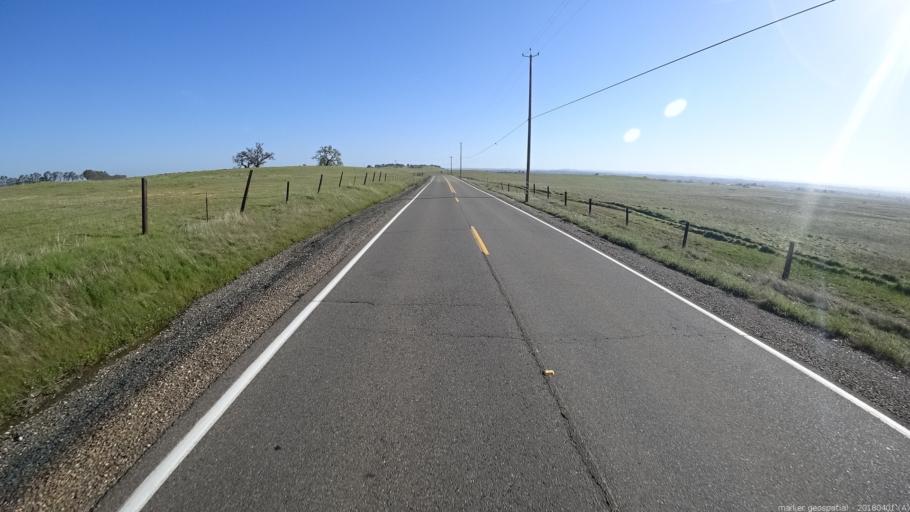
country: US
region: California
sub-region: Sacramento County
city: Rancho Murieta
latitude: 38.4306
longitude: -121.0515
